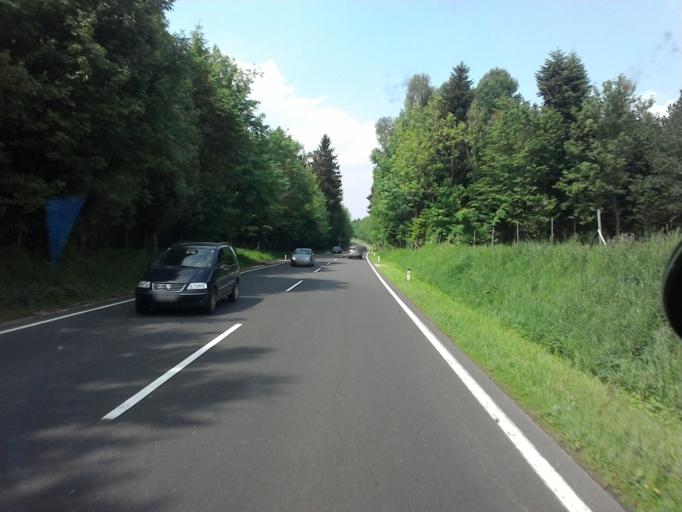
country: AT
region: Upper Austria
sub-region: Wels-Land
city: Sattledt
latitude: 48.0937
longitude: 14.0415
